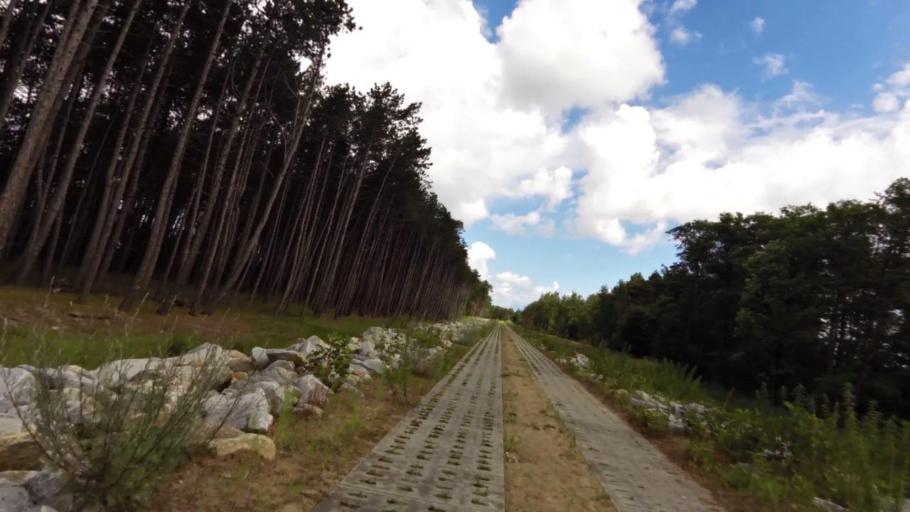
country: PL
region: West Pomeranian Voivodeship
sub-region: Powiat slawienski
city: Darlowo
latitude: 54.4870
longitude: 16.4343
